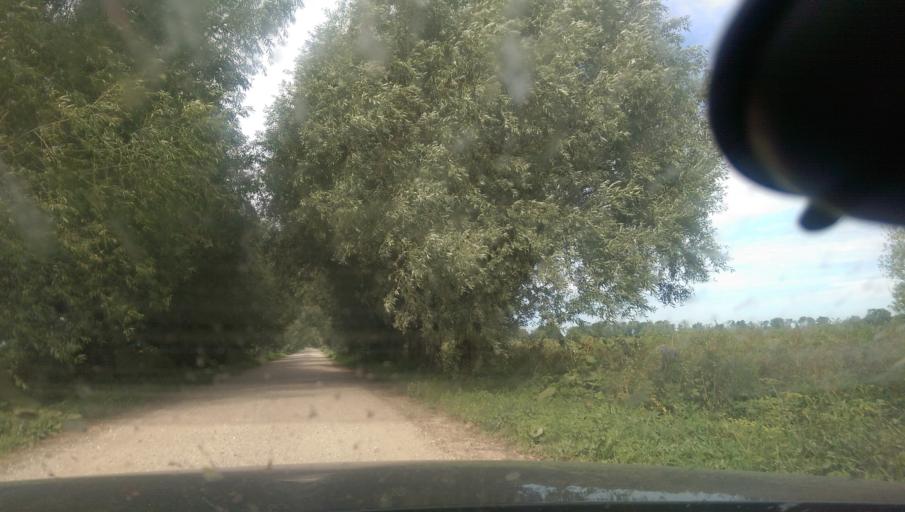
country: LT
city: Rusne
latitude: 55.2934
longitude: 21.3550
